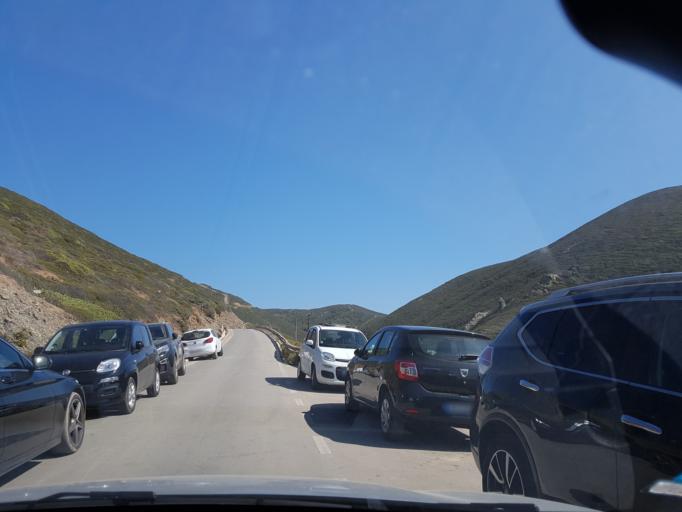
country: PT
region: Faro
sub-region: Vila do Bispo
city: Vila do Bispo
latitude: 37.1089
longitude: -8.9355
